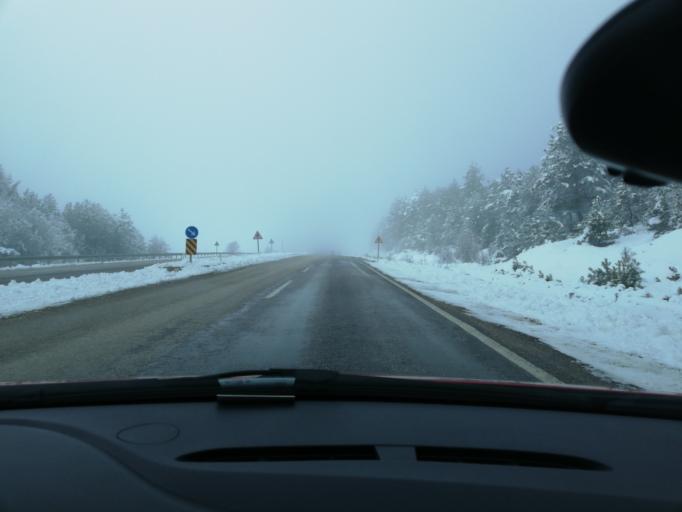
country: TR
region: Kastamonu
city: Akkaya
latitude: 41.2990
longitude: 33.5265
